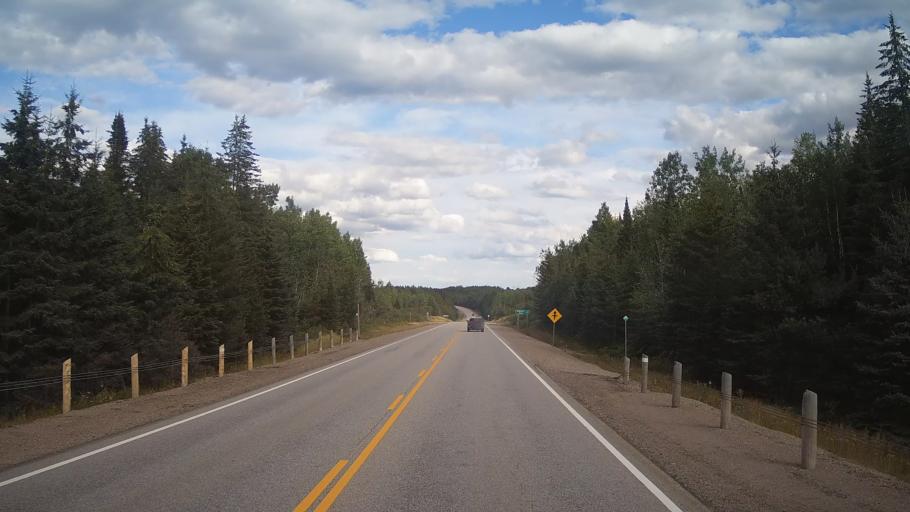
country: CA
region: Ontario
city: Mattawa
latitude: 46.2816
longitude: -78.4990
